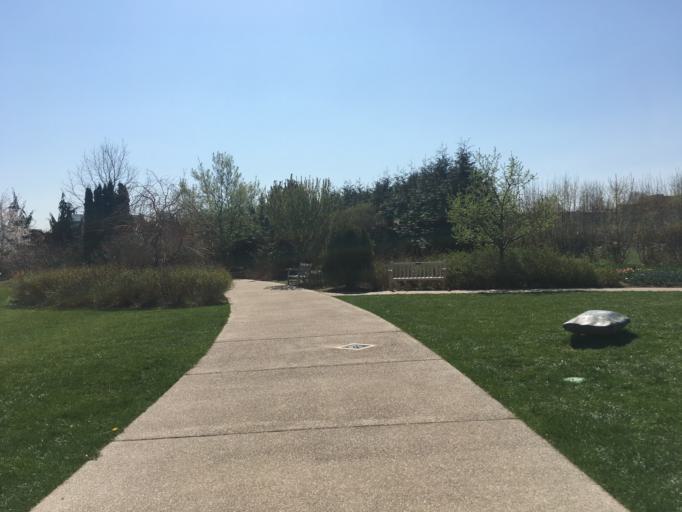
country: US
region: Pennsylvania
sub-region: Centre County
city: State College
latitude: 40.8059
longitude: -77.8688
